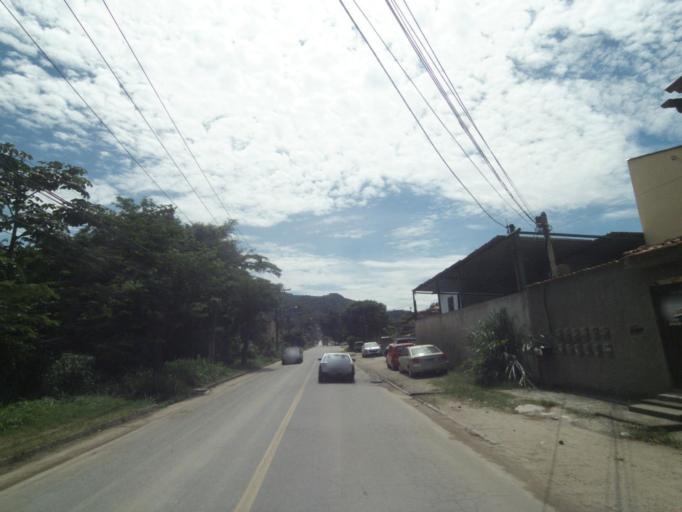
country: BR
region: Rio de Janeiro
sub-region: Niteroi
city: Niteroi
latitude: -22.9292
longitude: -43.0080
